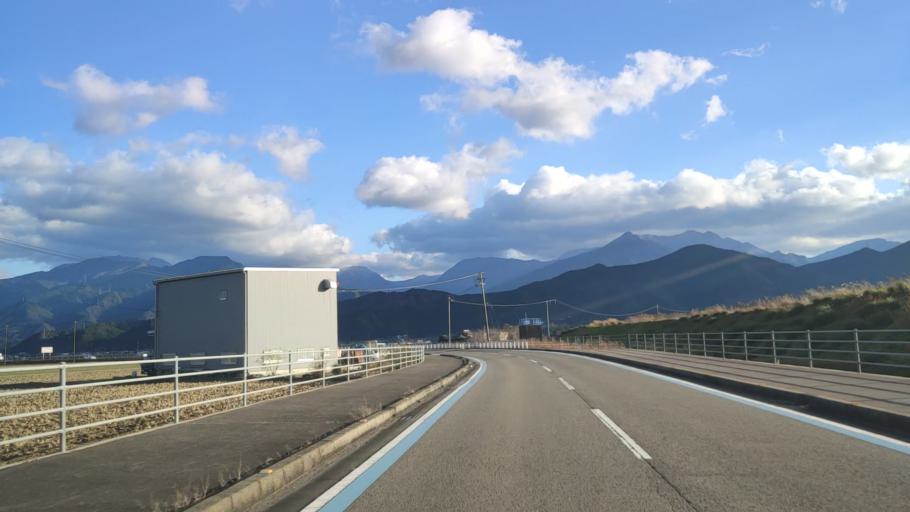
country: JP
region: Ehime
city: Saijo
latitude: 33.9081
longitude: 133.1425
